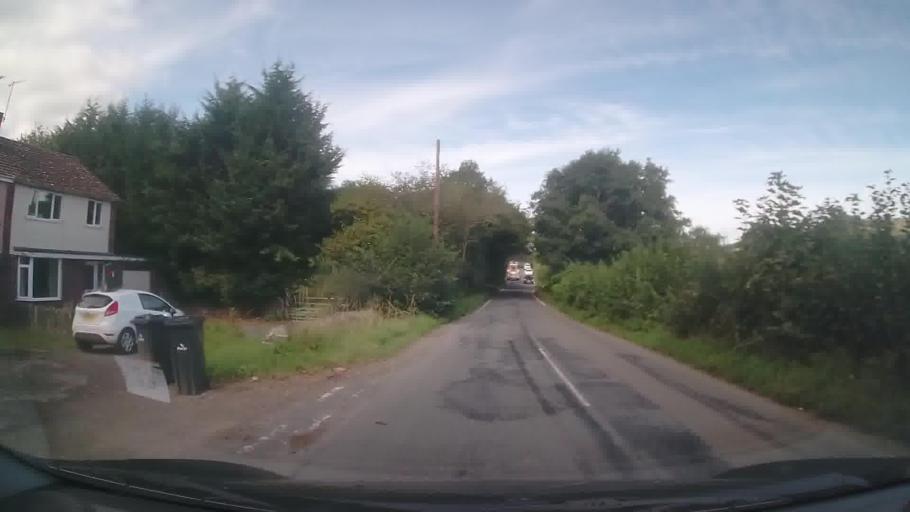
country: GB
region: Wales
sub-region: Sir Powys
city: Whitton
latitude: 52.2826
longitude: -3.0737
